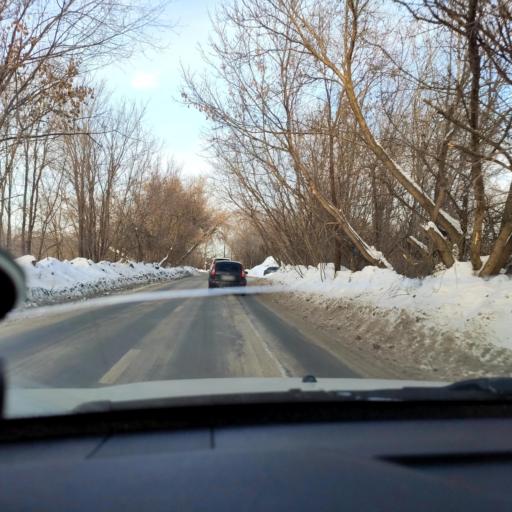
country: RU
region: Samara
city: Smyshlyayevka
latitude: 53.2497
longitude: 50.3675
